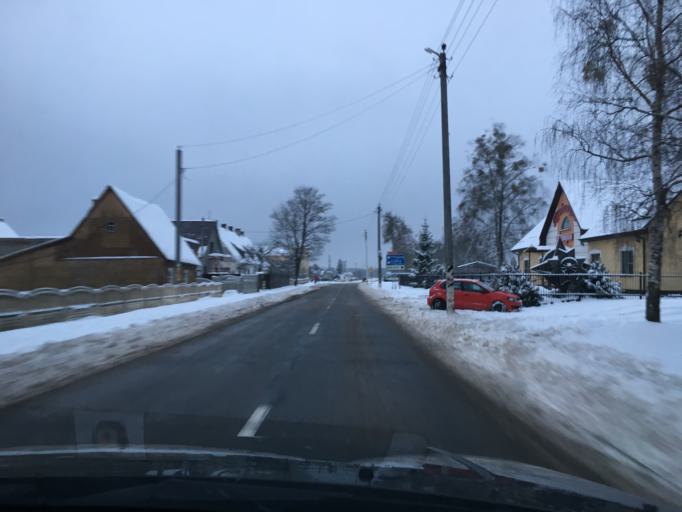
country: LT
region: Alytaus apskritis
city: Druskininkai
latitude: 53.8867
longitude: 24.1364
